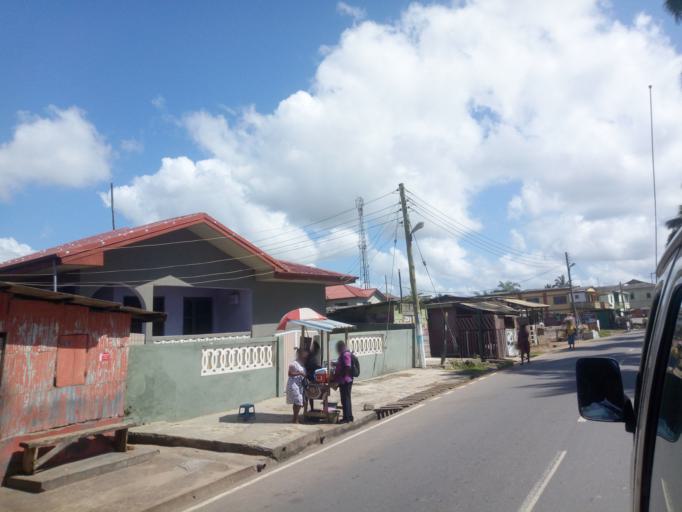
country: GH
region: Central
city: Elmina
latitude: 5.0902
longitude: -1.3462
